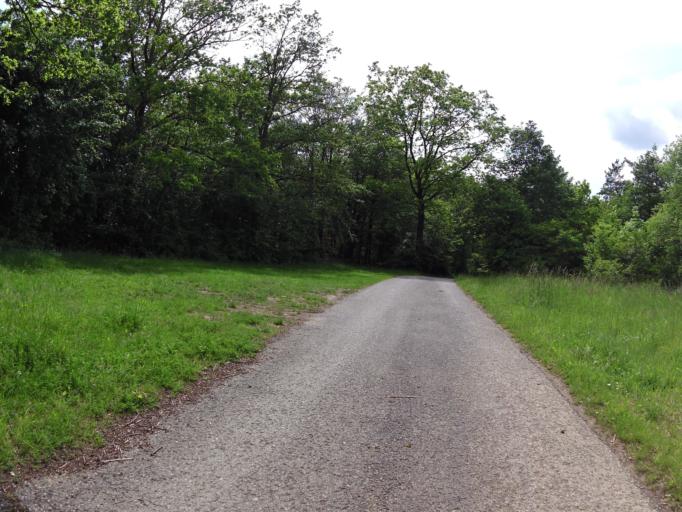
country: DE
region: Bavaria
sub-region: Regierungsbezirk Unterfranken
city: Winterhausen
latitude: 49.7191
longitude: 10.0181
